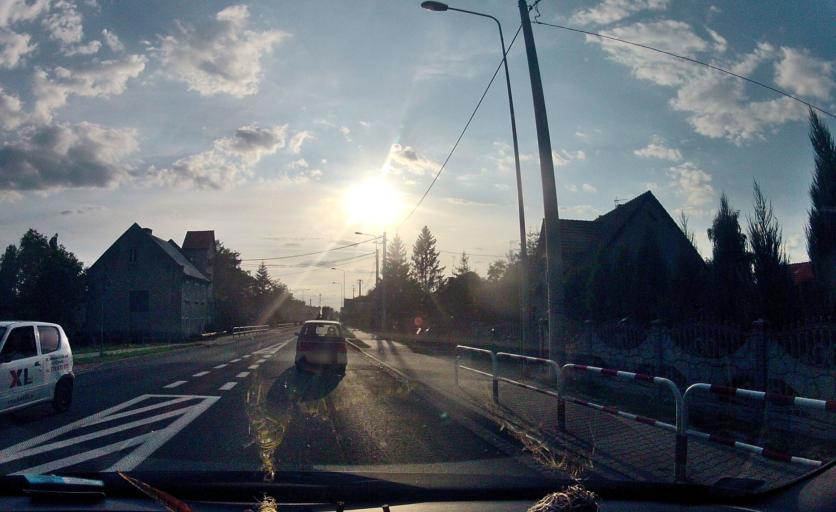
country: PL
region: Opole Voivodeship
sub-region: Powiat kluczborski
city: Kluczbork
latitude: 50.9740
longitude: 18.2434
